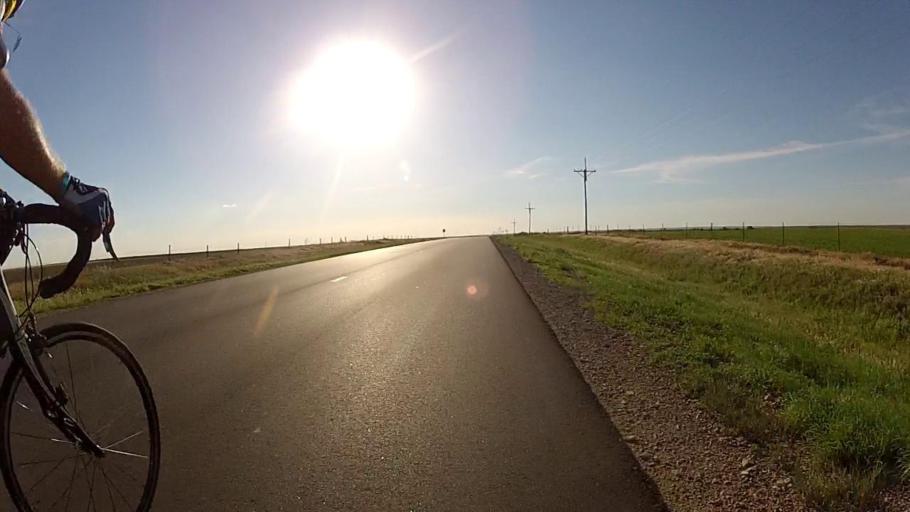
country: US
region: Kansas
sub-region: Comanche County
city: Coldwater
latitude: 37.2821
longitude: -99.1149
